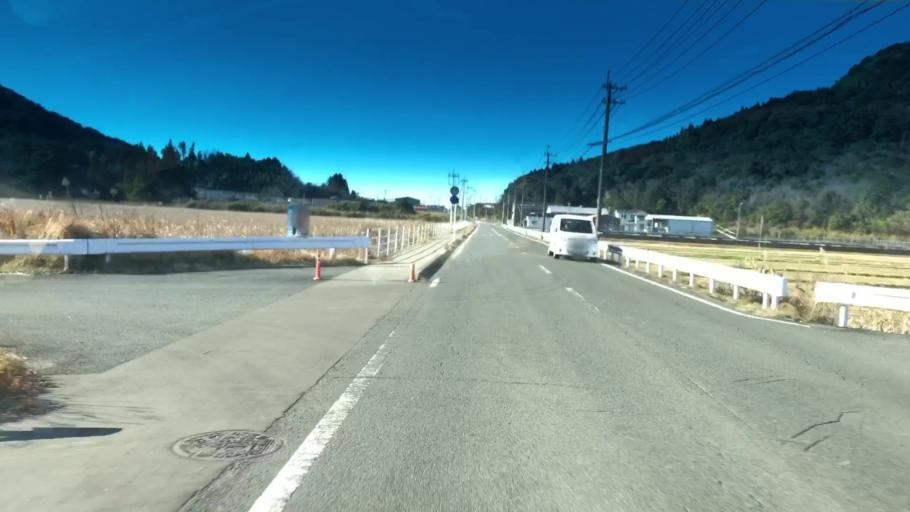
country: JP
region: Kagoshima
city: Satsumasendai
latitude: 31.8179
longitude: 130.2686
